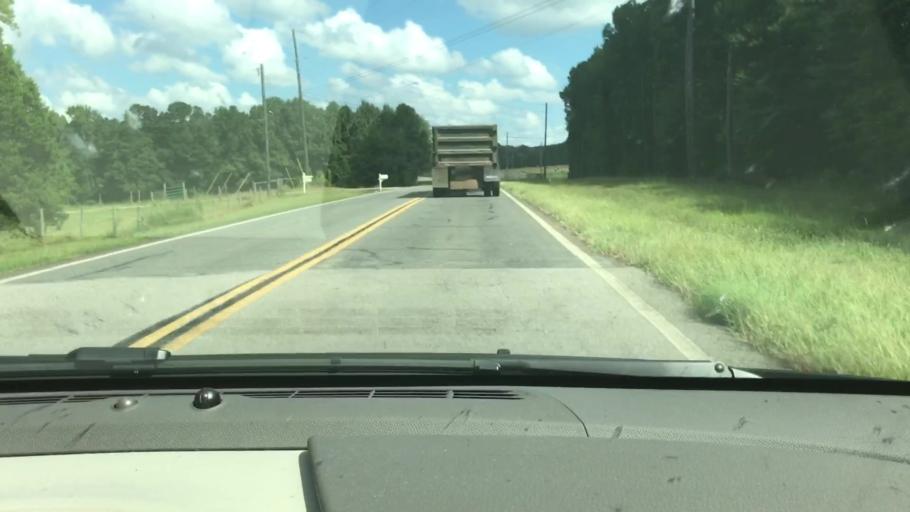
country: US
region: Alabama
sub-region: Chambers County
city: Valley
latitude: 32.8473
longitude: -85.0355
